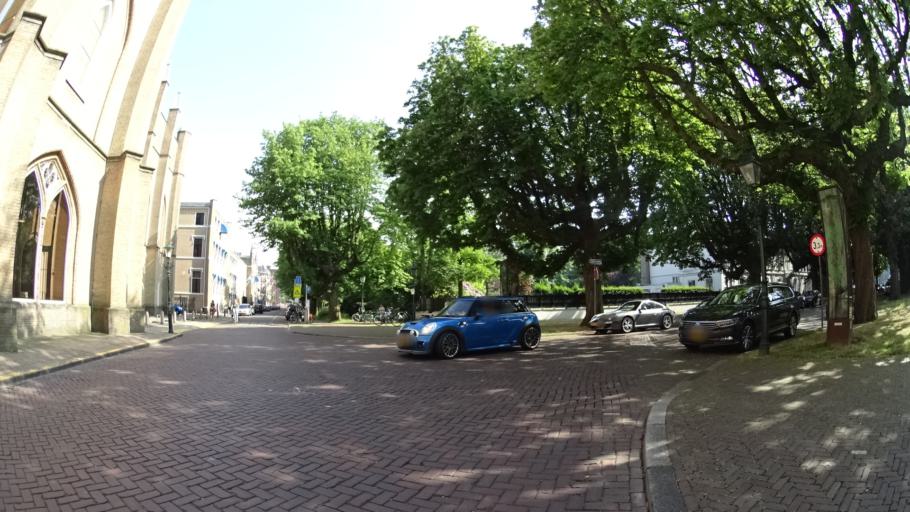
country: NL
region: South Holland
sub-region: Gemeente Den Haag
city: The Hague
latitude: 52.0872
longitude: 4.3073
